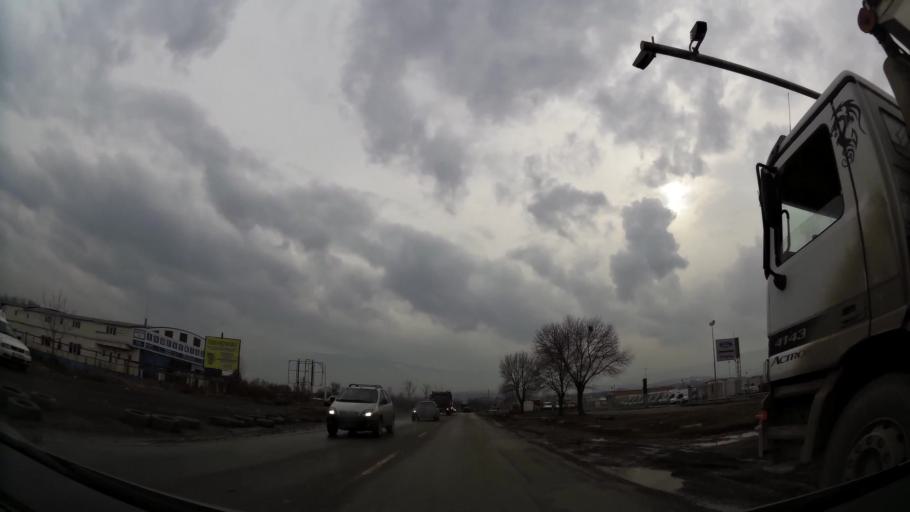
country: BG
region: Sofiya
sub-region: Obshtina Bozhurishte
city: Bozhurishte
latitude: 42.7058
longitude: 23.2303
